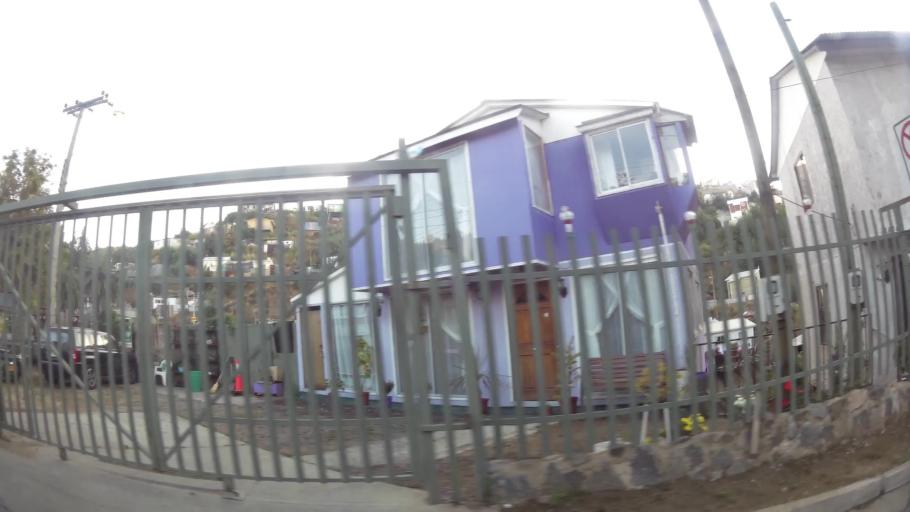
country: CL
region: Valparaiso
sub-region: Provincia de Valparaiso
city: Valparaiso
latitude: -33.0611
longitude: -71.6047
